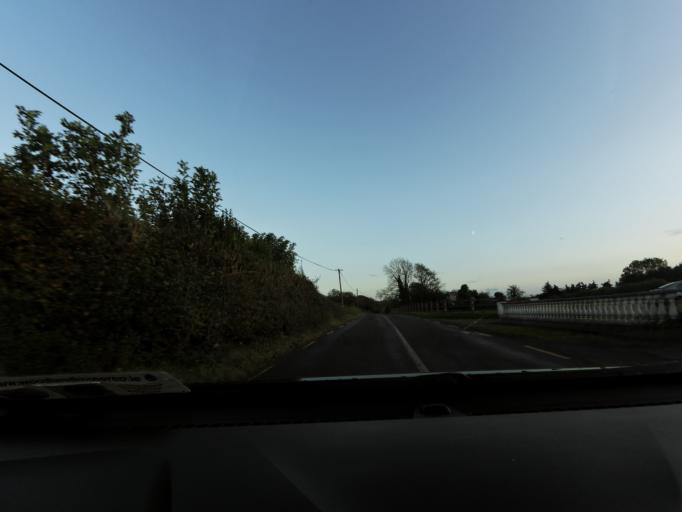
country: IE
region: Connaught
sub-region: County Galway
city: Tuam
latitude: 53.5135
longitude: -8.6128
